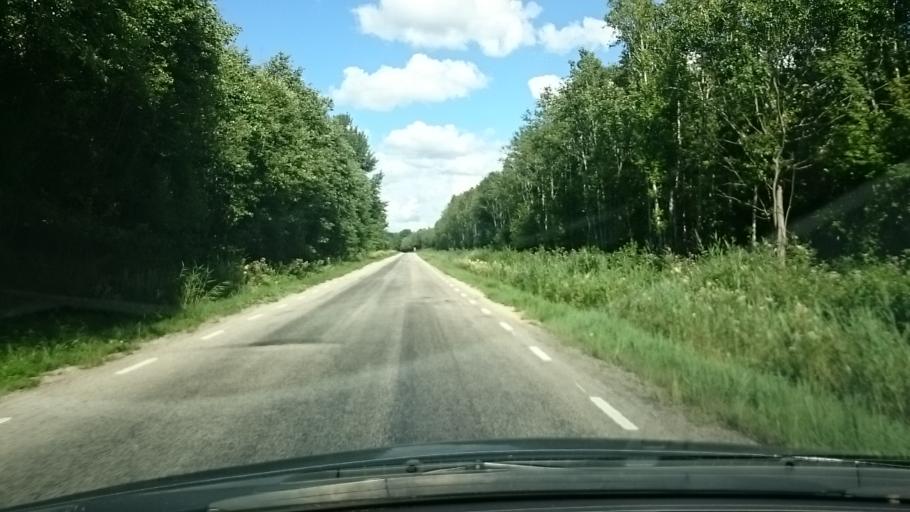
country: EE
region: Laeaene
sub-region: Ridala Parish
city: Uuemoisa
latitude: 59.0648
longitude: 23.5752
